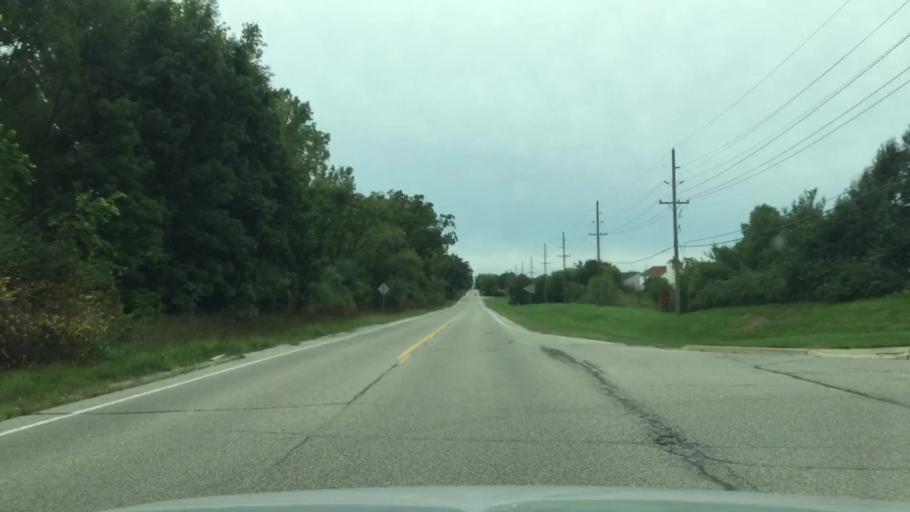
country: US
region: Michigan
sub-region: Washtenaw County
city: Ypsilanti
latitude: 42.2152
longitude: -83.6601
